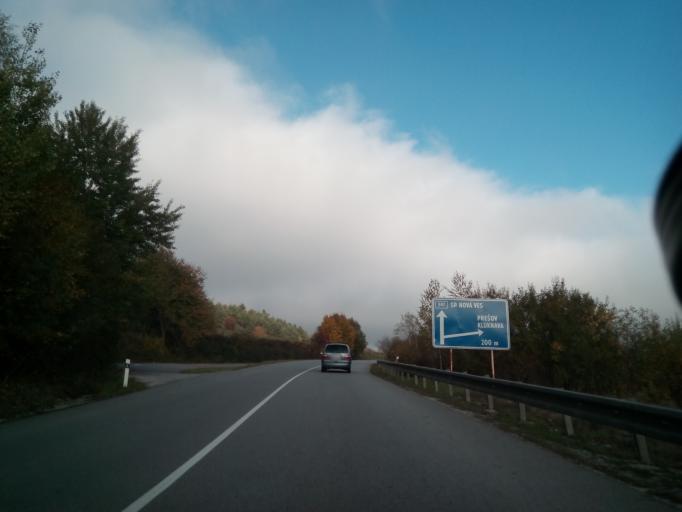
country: SK
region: Kosicky
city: Krompachy
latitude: 48.9162
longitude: 20.9337
